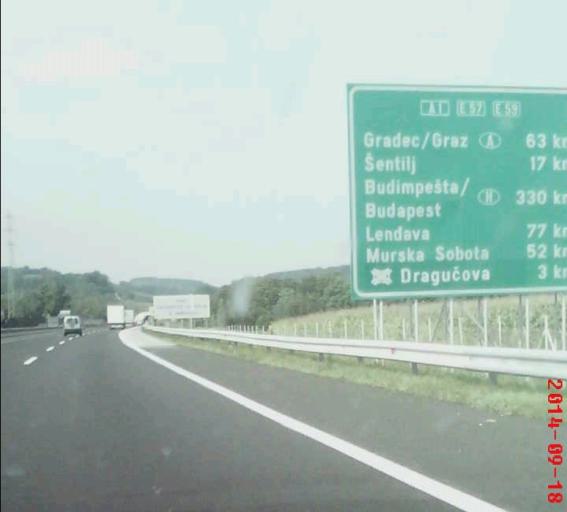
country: SI
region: Miklavz na Dravskem Polju
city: Miklavz na Dravskem Polju
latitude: 46.5471
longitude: 15.6937
